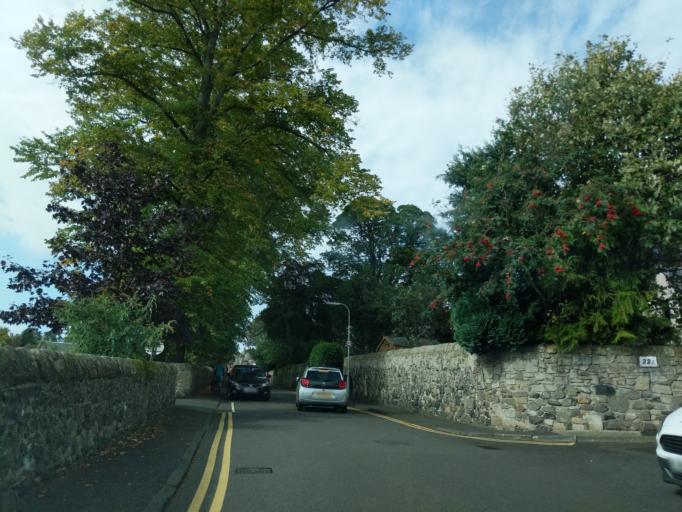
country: GB
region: Scotland
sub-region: Fife
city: Aberdour
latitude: 56.0524
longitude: -3.2999
